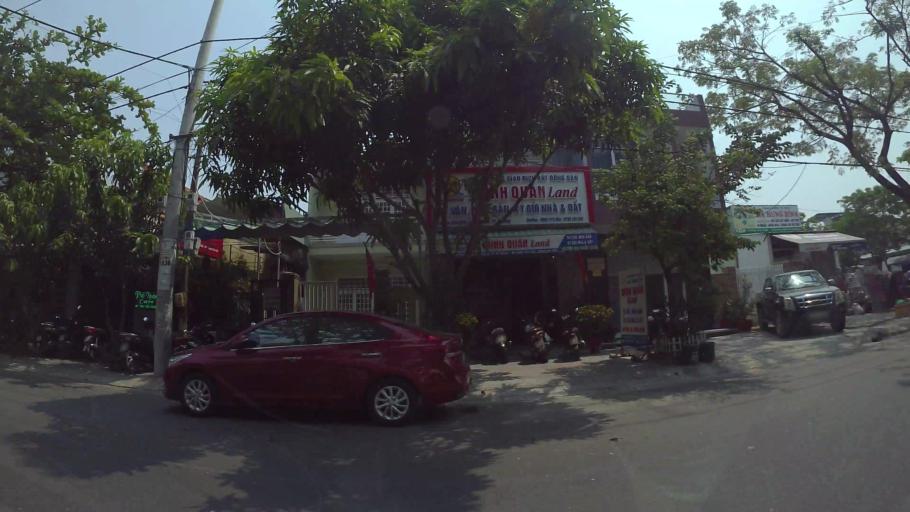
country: VN
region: Da Nang
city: Cam Le
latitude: 16.0011
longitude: 108.2131
